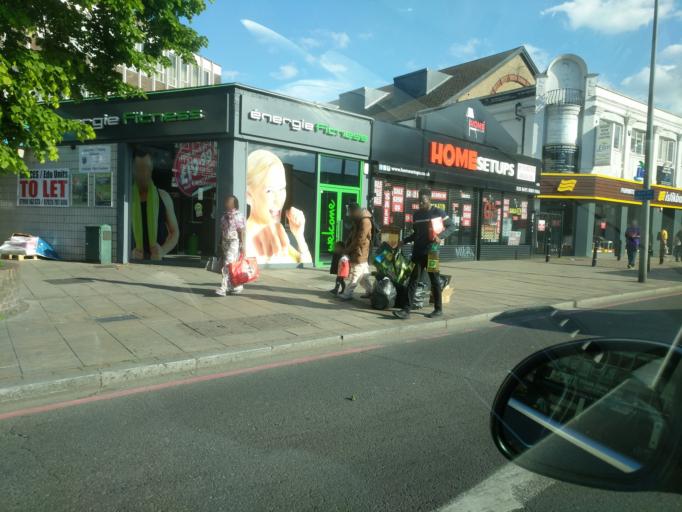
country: GB
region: England
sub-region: Greater London
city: Catford
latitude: 51.4485
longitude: -0.0171
